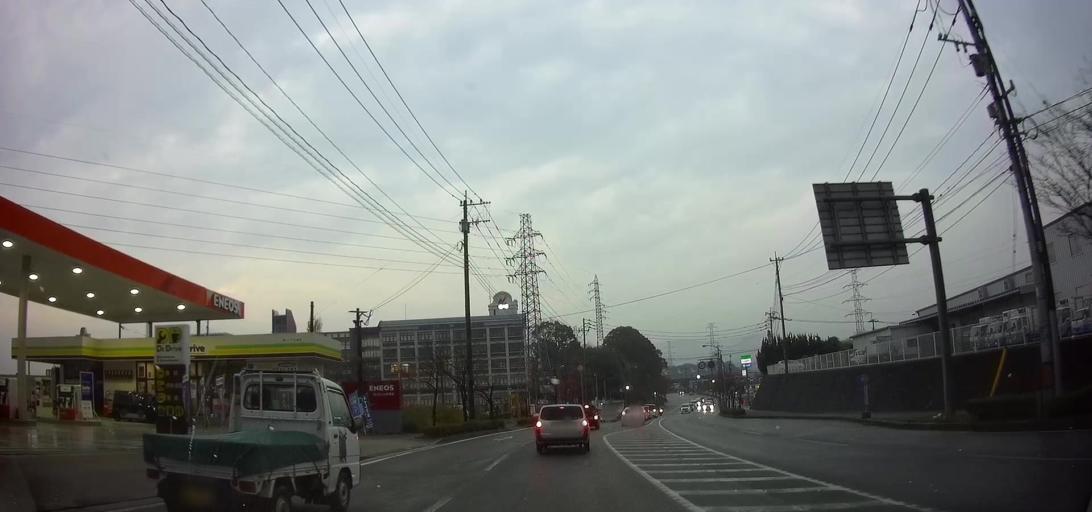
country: JP
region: Nagasaki
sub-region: Isahaya-shi
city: Isahaya
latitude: 32.8391
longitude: 130.0136
